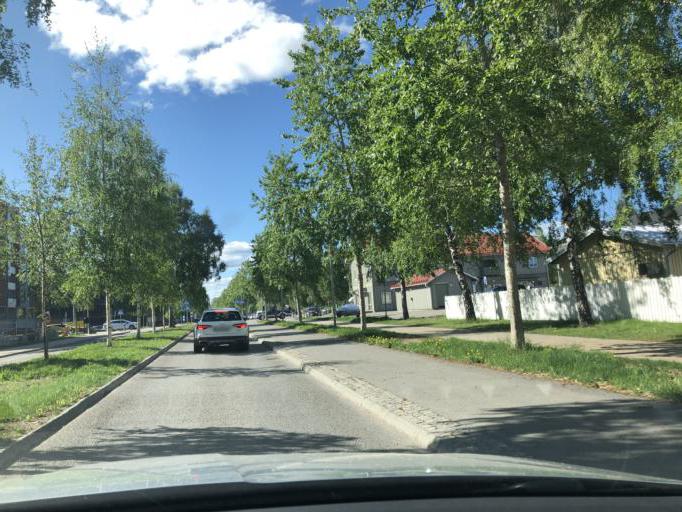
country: SE
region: Norrbotten
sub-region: Pitea Kommun
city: Pitea
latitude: 65.3166
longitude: 21.4869
